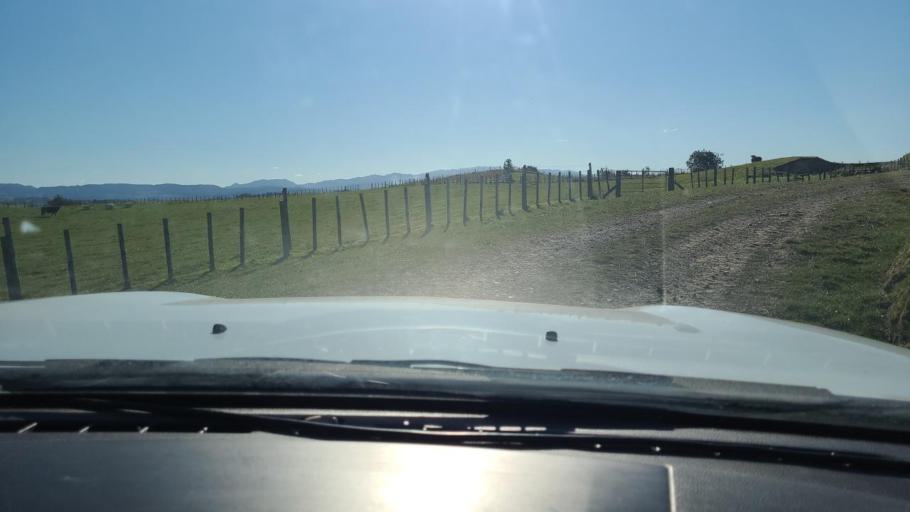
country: NZ
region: Hawke's Bay
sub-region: Napier City
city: Taradale
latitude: -39.4582
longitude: 176.6236
